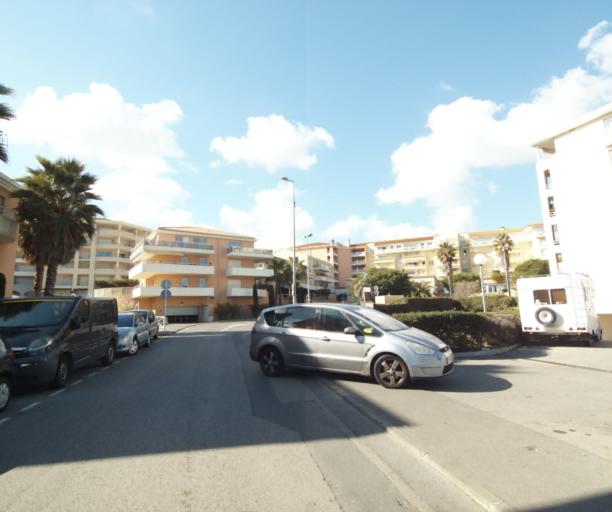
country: FR
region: Provence-Alpes-Cote d'Azur
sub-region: Departement des Alpes-Maritimes
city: Antibes
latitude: 43.5728
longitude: 7.0918
